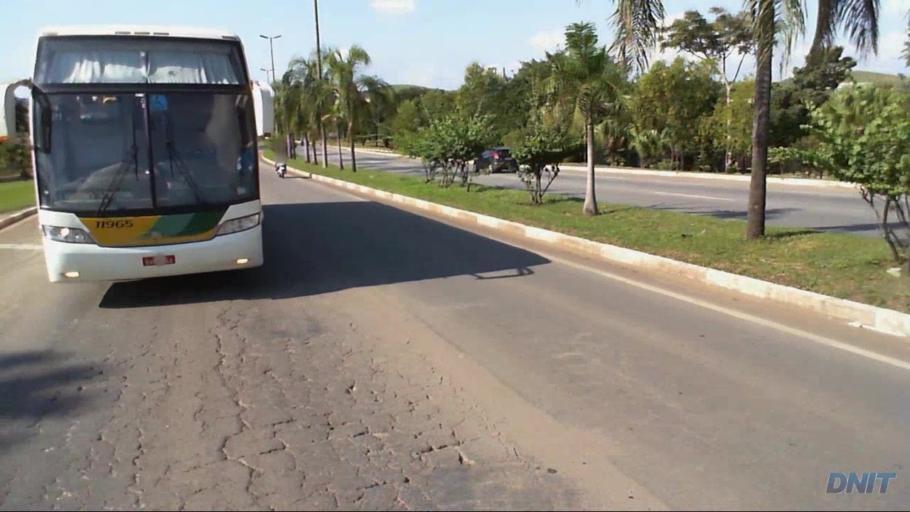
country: BR
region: Minas Gerais
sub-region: Ipatinga
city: Ipatinga
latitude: -19.4728
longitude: -42.5411
